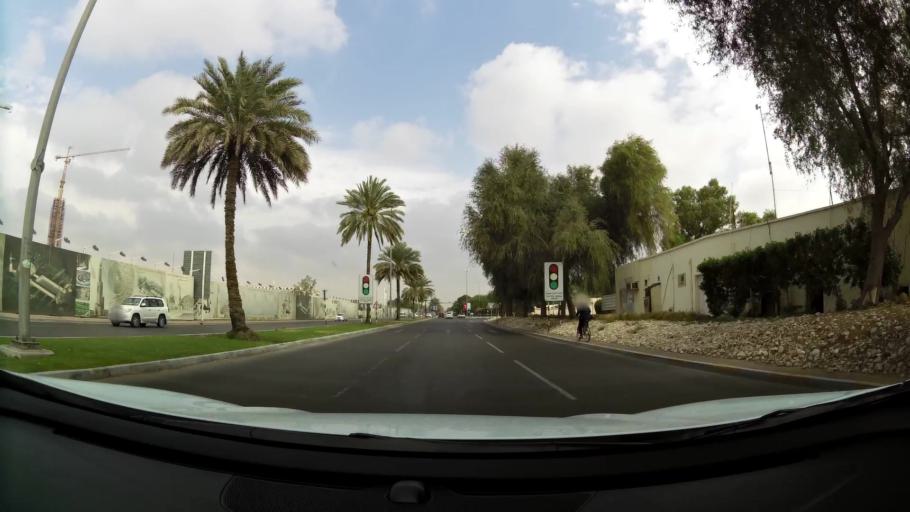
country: AE
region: Abu Dhabi
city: Al Ain
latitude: 24.2250
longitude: 55.7511
